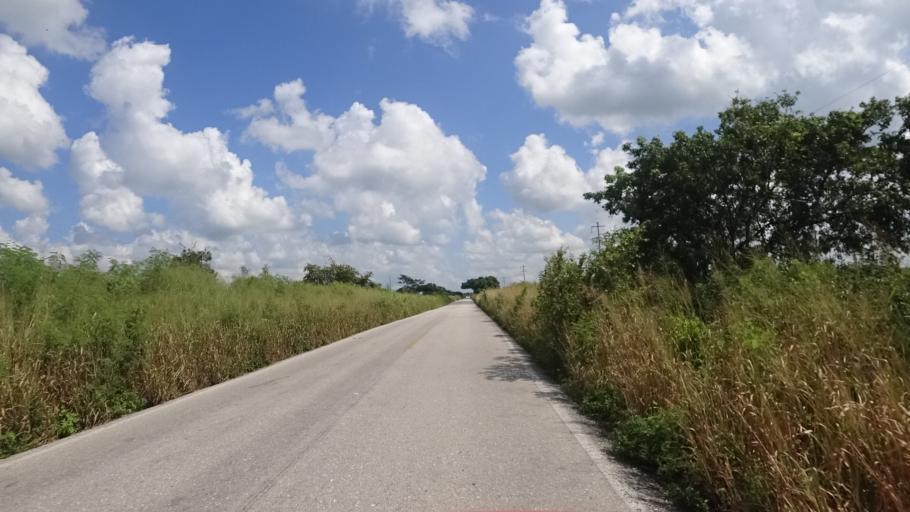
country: MX
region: Yucatan
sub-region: Panaba
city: Loche
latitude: 21.3542
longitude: -88.1494
